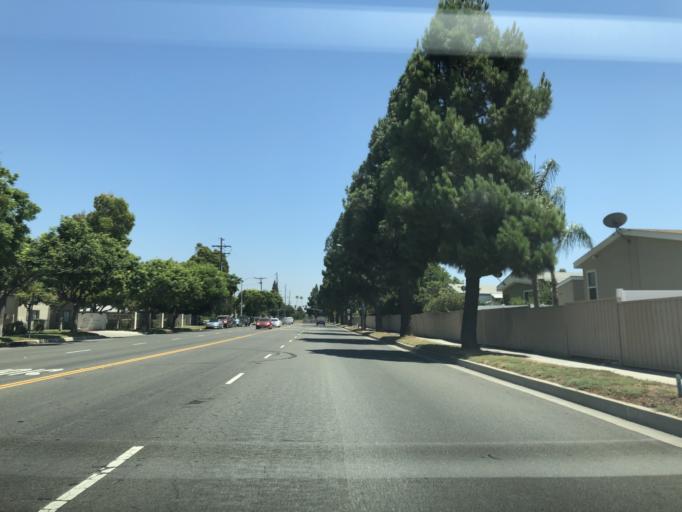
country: US
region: California
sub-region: Riverside County
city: Corona
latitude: 33.8755
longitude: -117.5914
